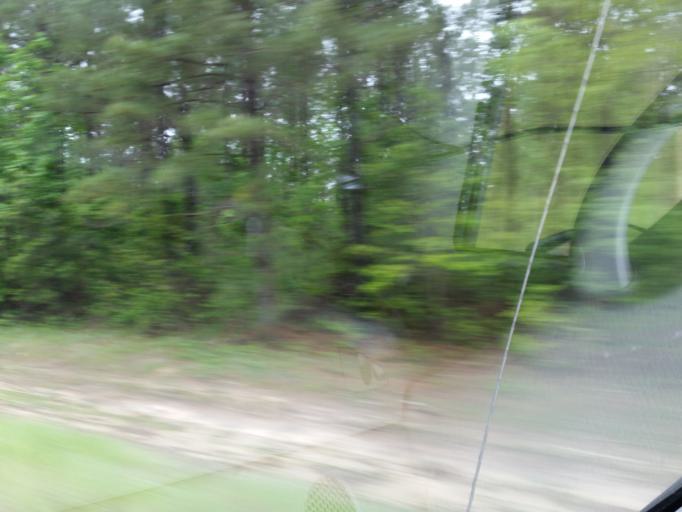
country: US
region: Georgia
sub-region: Crawford County
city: Knoxville
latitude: 32.6868
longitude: -83.9183
